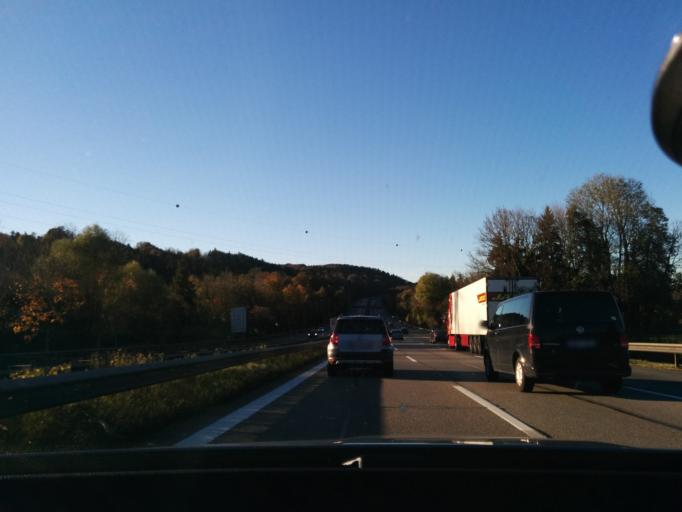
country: DE
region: Bavaria
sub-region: Upper Bavaria
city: Irschenberg
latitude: 47.8324
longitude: 11.8843
